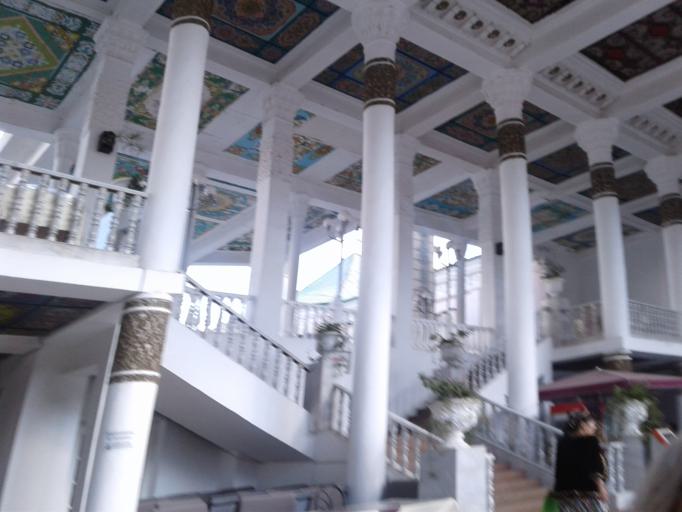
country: TJ
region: Dushanbe
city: Dushanbe
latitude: 38.5846
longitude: 68.7871
